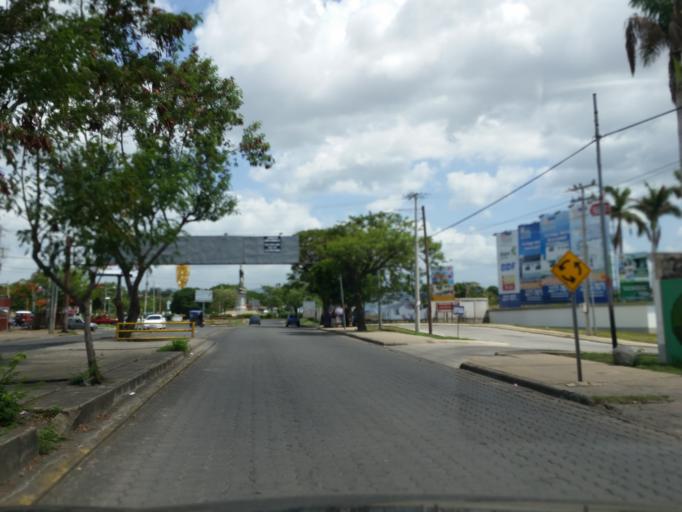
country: NI
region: Managua
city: Managua
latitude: 12.1453
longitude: -86.2243
